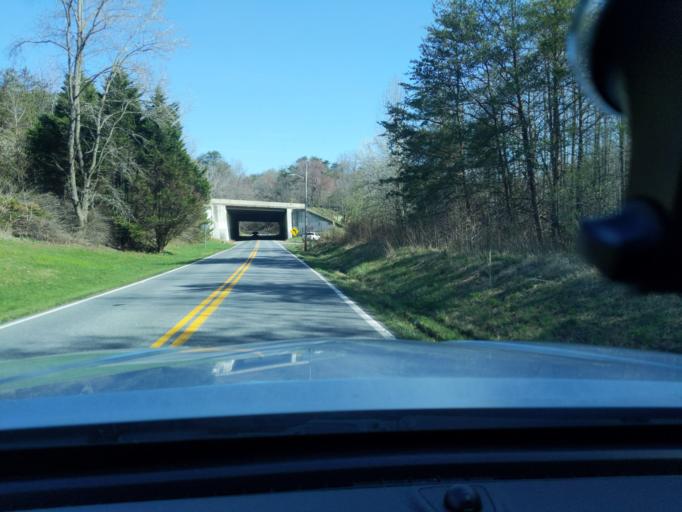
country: US
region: Maryland
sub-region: Anne Arundel County
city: Davidsonville
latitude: 38.9636
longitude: -76.6337
